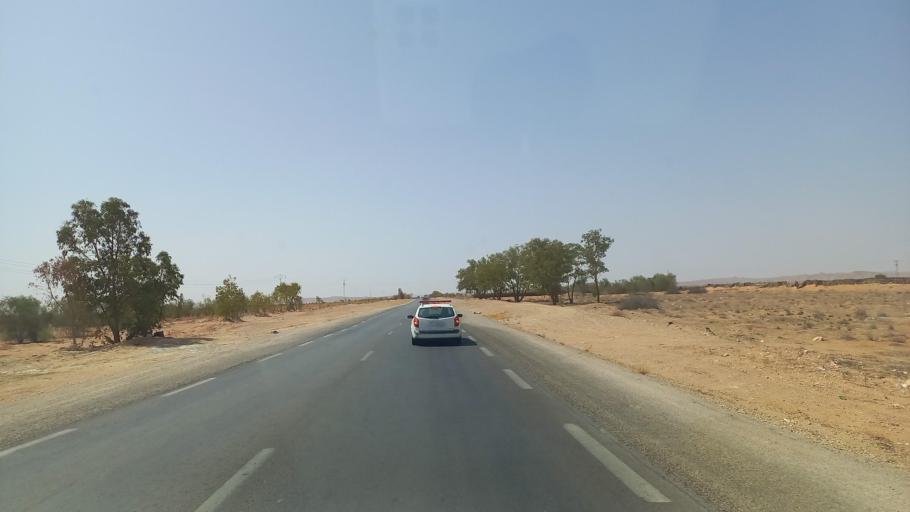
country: TN
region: Madanin
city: Medenine
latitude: 33.2224
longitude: 10.4503
